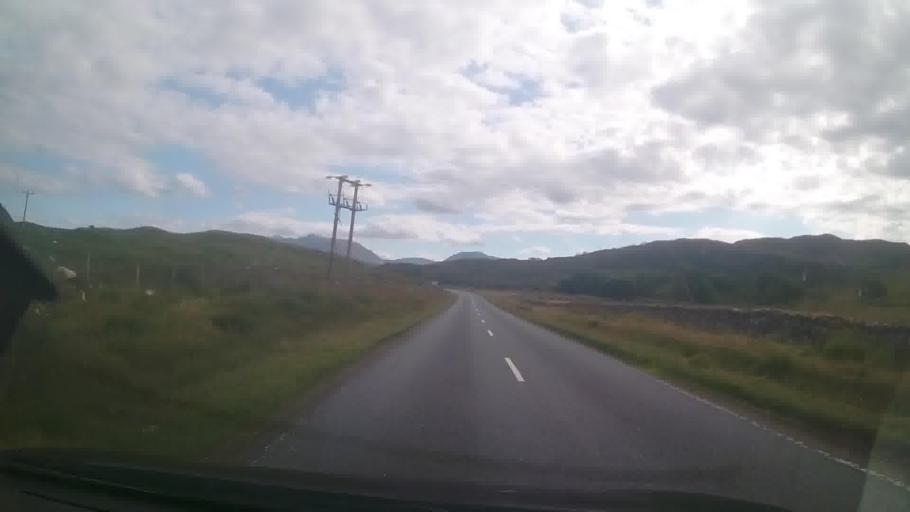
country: GB
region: Scotland
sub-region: Argyll and Bute
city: Oban
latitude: 56.6820
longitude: -5.3797
